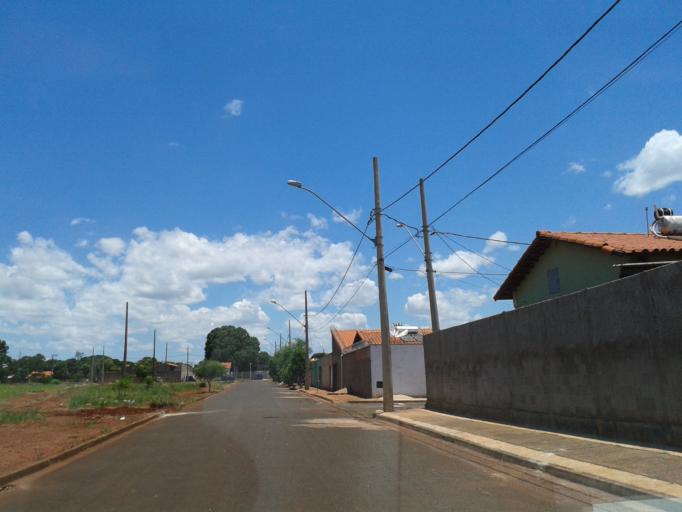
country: BR
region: Minas Gerais
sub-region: Centralina
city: Centralina
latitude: -18.7154
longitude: -49.2043
